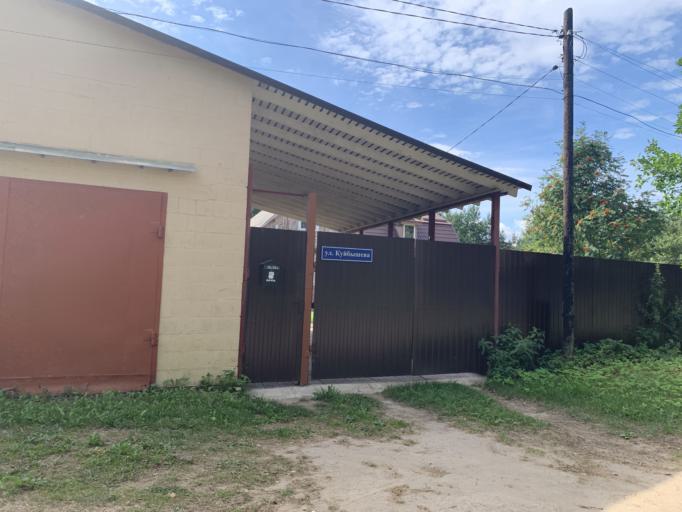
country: RU
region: Moskovskaya
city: Mamontovka
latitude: 55.9844
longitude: 37.8107
